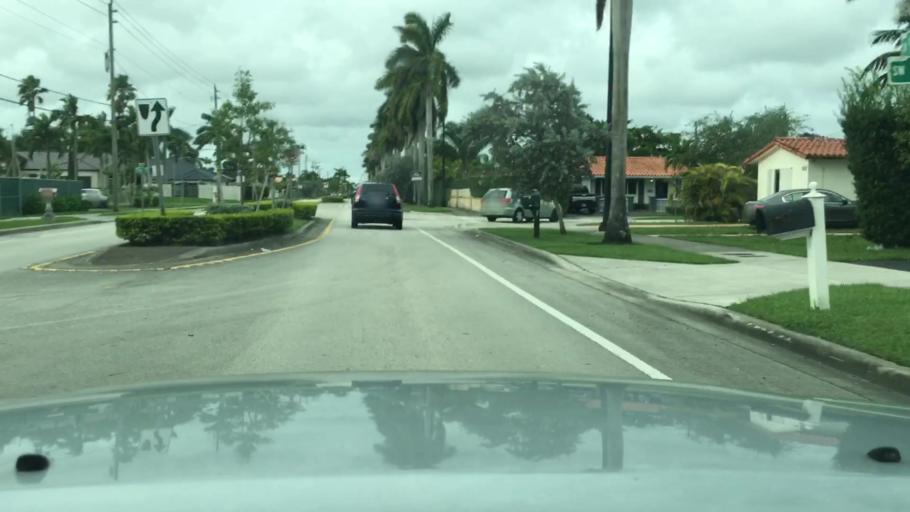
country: US
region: Florida
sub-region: Miami-Dade County
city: Sunset
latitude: 25.7126
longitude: -80.3507
